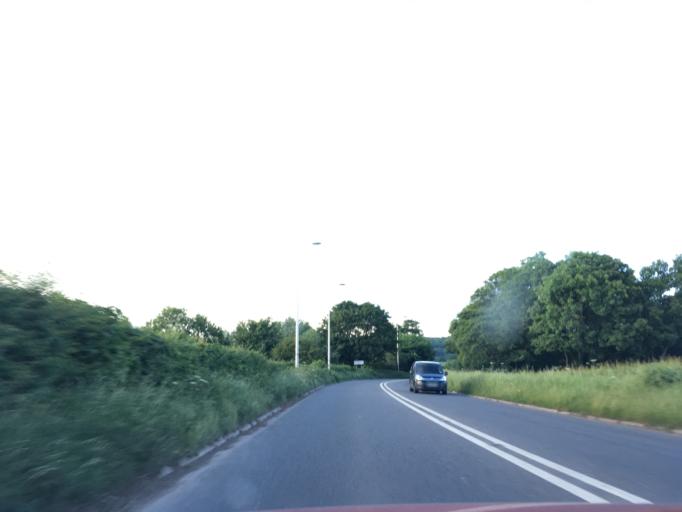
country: GB
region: England
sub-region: North Somerset
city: Burrington
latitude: 51.3499
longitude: -2.7482
